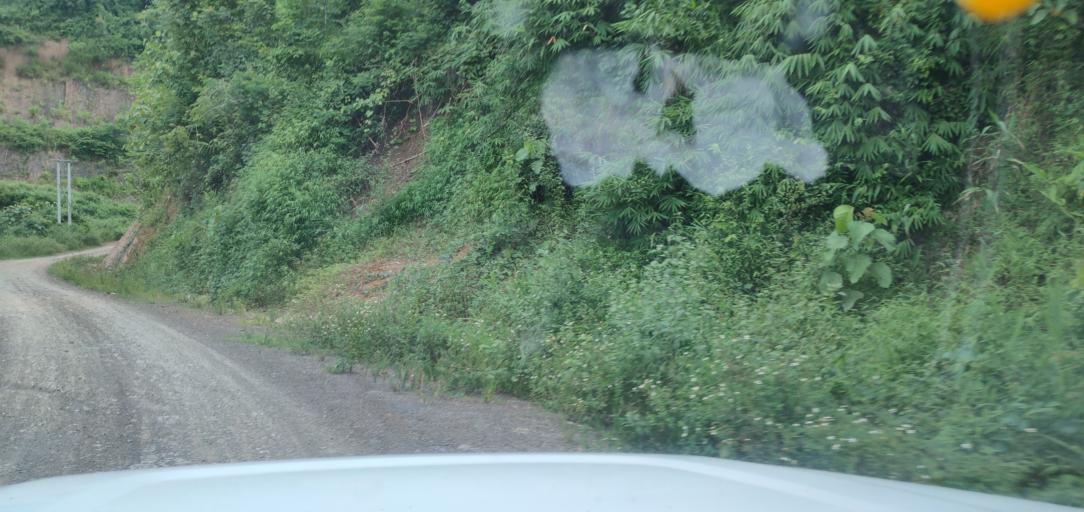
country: VN
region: Huyen Dien Bien
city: Dien Bien Phu
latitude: 21.3342
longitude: 102.7189
